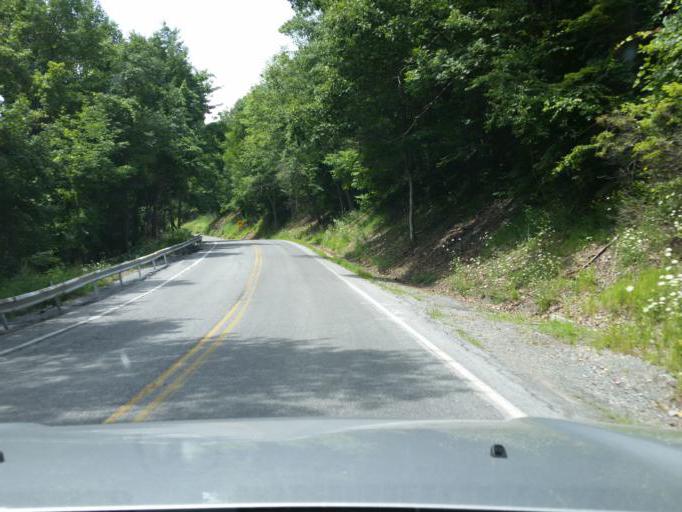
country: US
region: Pennsylvania
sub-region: Blair County
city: Altoona
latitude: 40.5559
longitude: -78.4507
